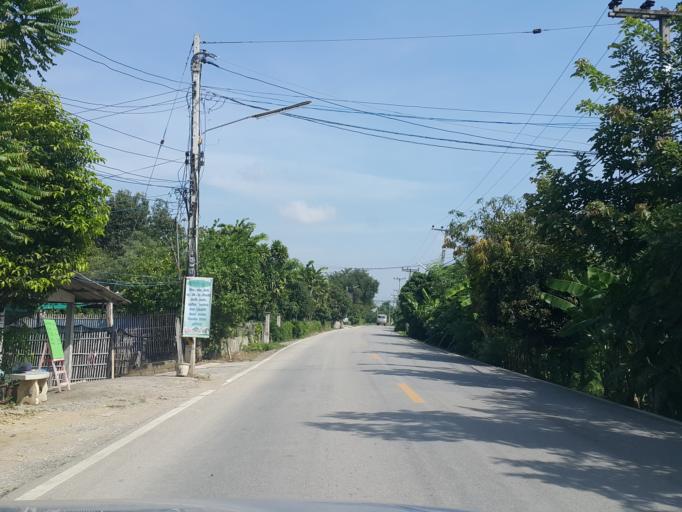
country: TH
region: Chiang Mai
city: Saraphi
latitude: 18.6858
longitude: 99.0611
